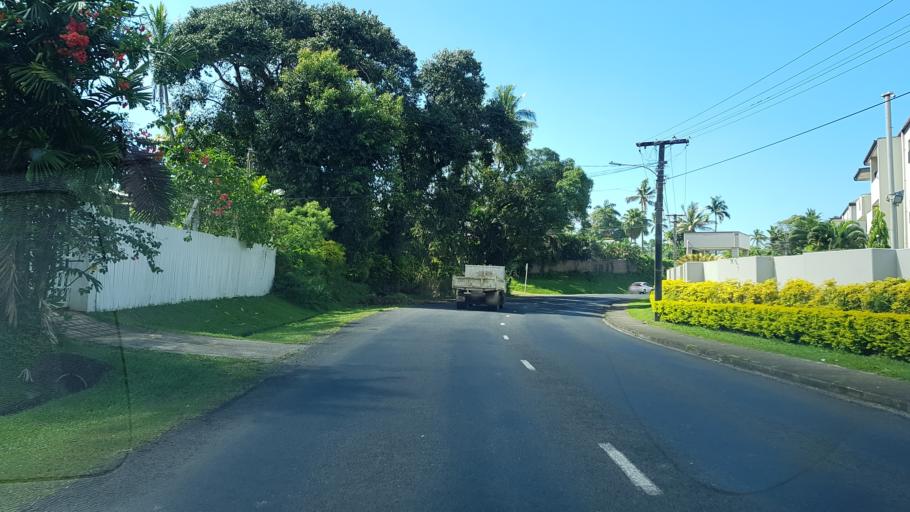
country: FJ
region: Central
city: Suva
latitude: -18.1453
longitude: 178.4540
